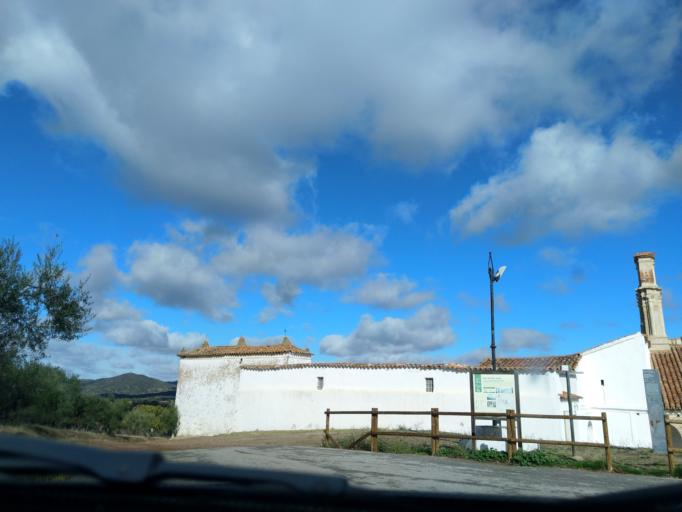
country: ES
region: Extremadura
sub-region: Provincia de Badajoz
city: Reina
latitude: 38.1311
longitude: -5.9402
